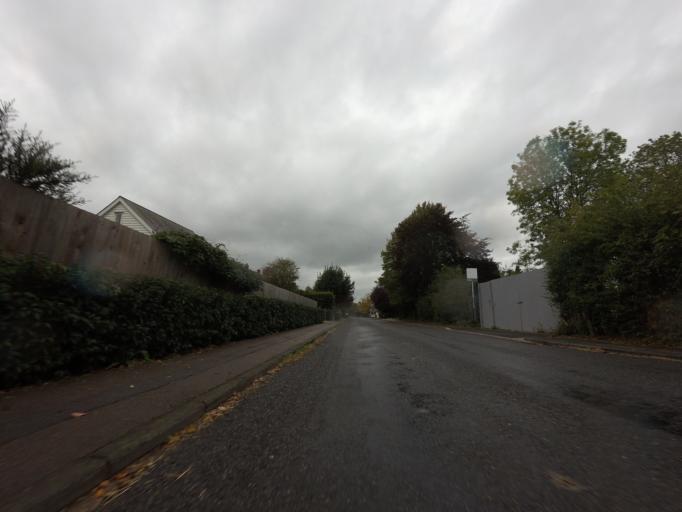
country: GB
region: England
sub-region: Cambridgeshire
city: Comberton
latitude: 52.1630
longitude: -0.0070
